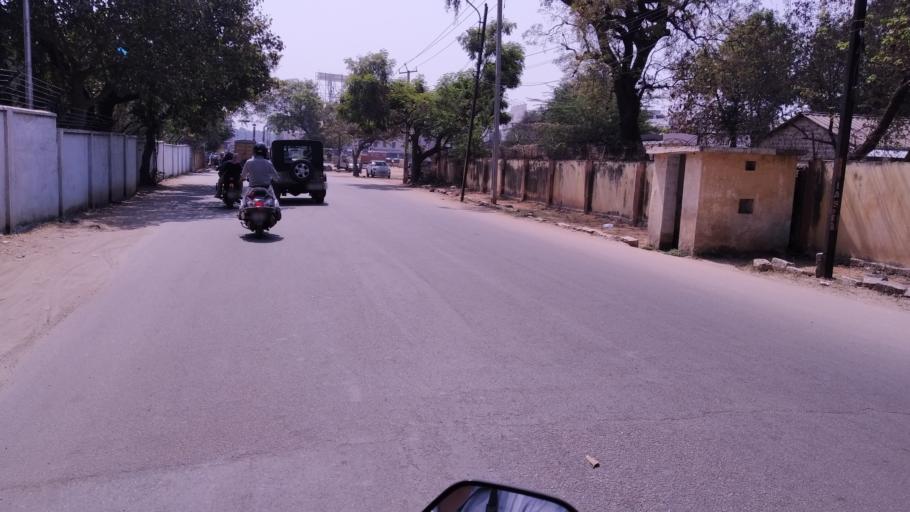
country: IN
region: Telangana
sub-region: Hyderabad
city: Malkajgiri
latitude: 17.4584
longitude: 78.4849
